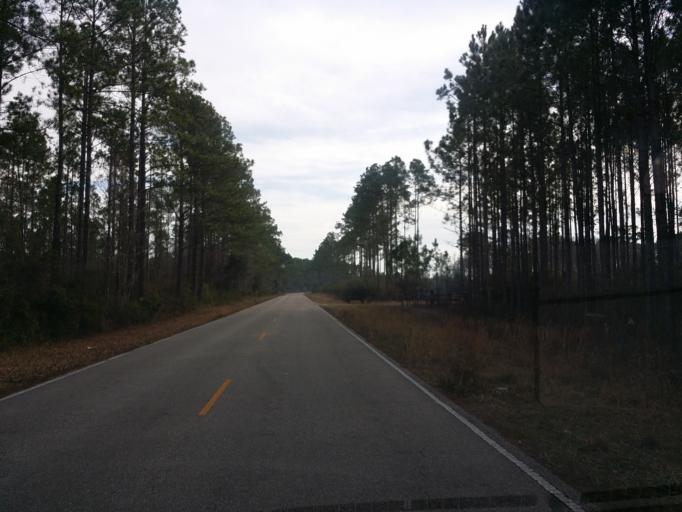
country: US
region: Florida
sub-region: Leon County
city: Woodville
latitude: 30.1799
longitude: -84.1637
